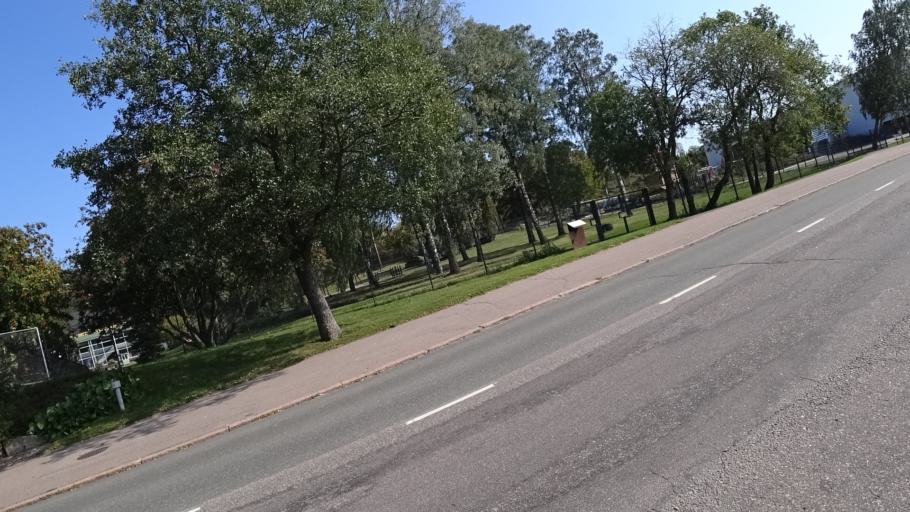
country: FI
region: Kymenlaakso
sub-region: Kotka-Hamina
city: Kotka
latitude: 60.4563
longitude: 26.9368
